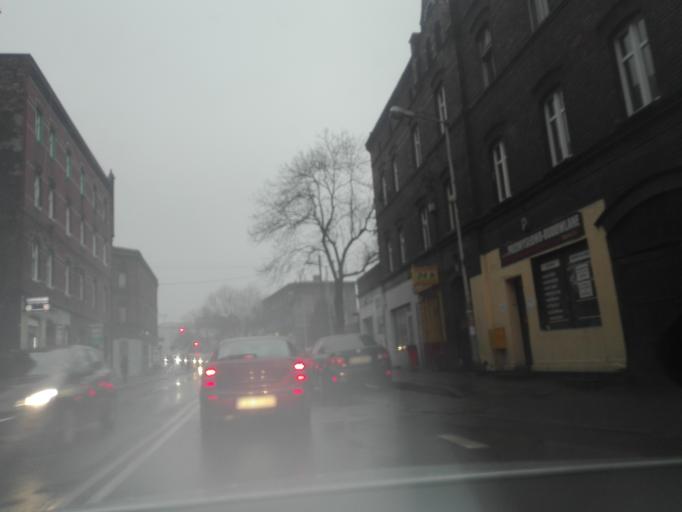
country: PL
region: Silesian Voivodeship
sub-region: Katowice
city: Katowice
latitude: 50.2695
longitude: 19.0364
